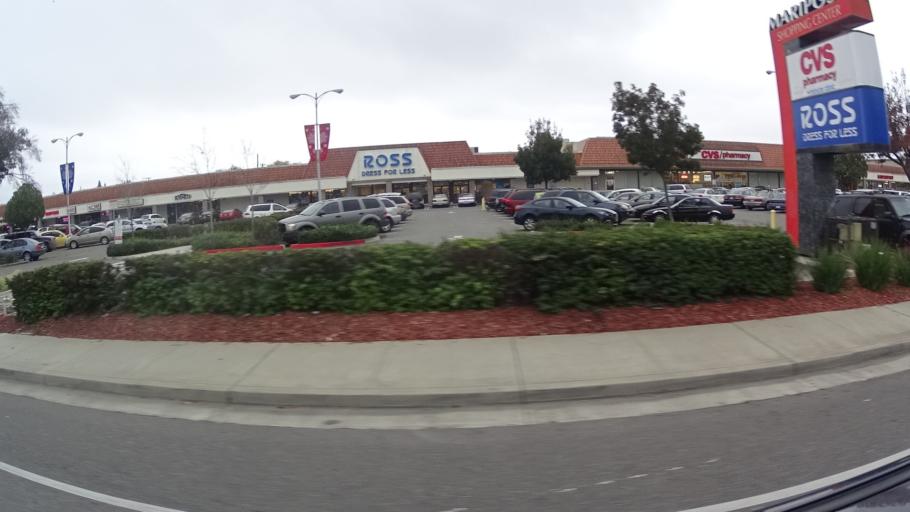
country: US
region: California
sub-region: Santa Clara County
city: Santa Clara
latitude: 37.3391
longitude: -121.9742
